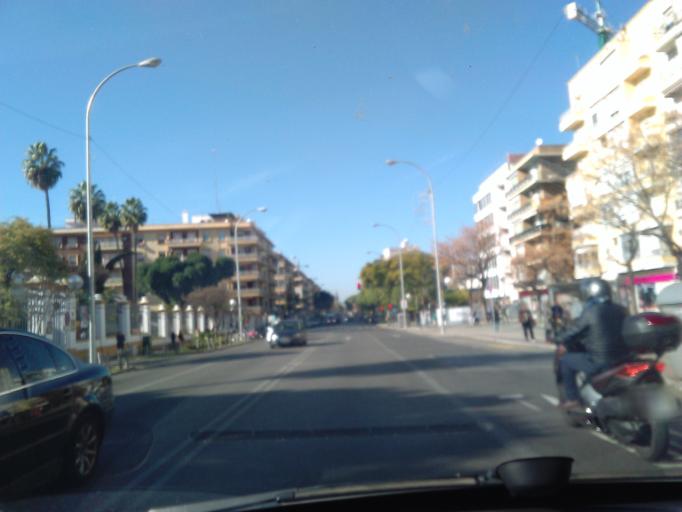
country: ES
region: Andalusia
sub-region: Provincia de Sevilla
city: Sevilla
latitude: 37.3820
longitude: -5.9685
